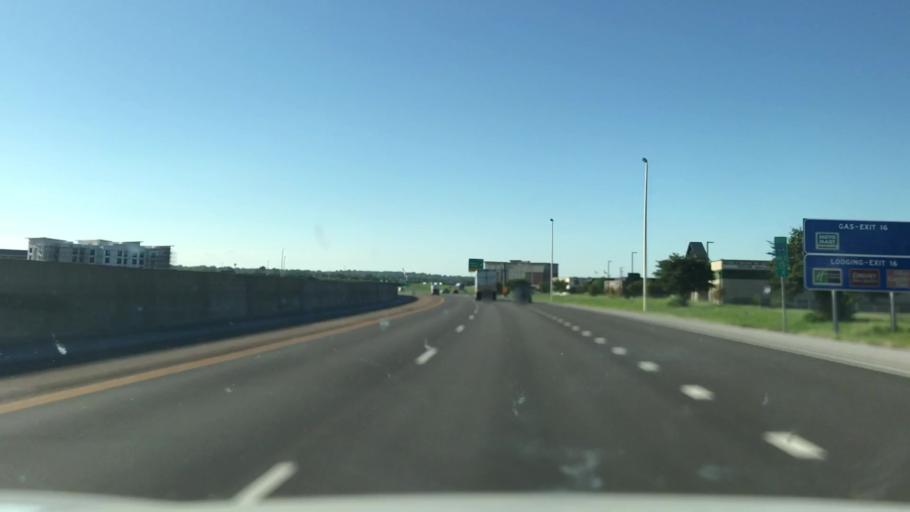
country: US
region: Illinois
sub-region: Saint Clair County
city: O'Fallon
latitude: 38.5802
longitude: -89.9351
